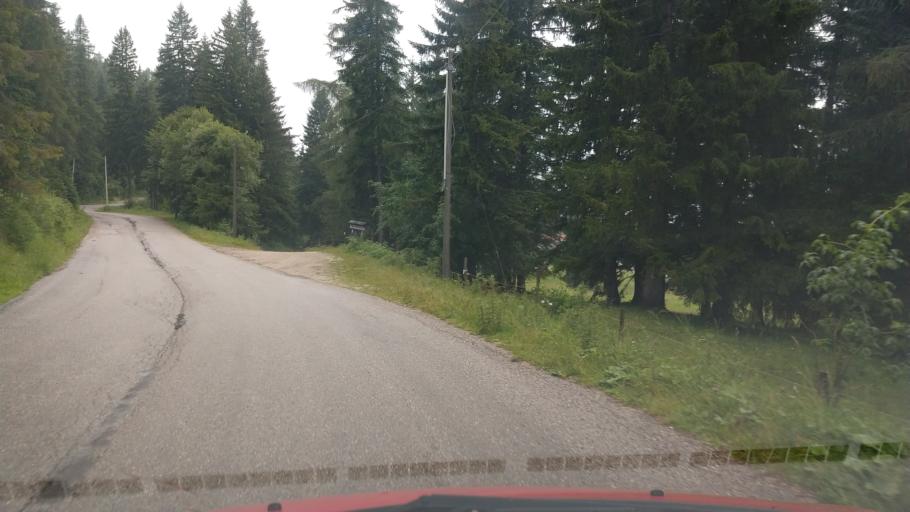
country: IT
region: Veneto
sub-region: Provincia di Vicenza
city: Lastebasse
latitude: 45.8981
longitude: 11.2623
